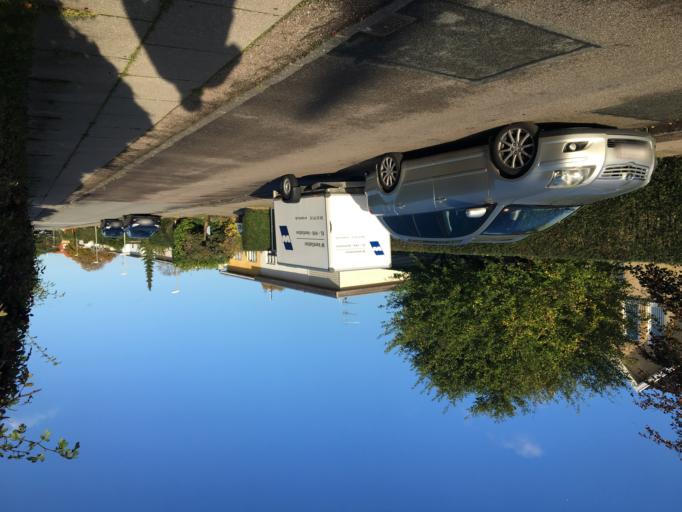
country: DK
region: Capital Region
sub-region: Tarnby Kommune
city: Tarnby
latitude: 55.6423
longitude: 12.6276
